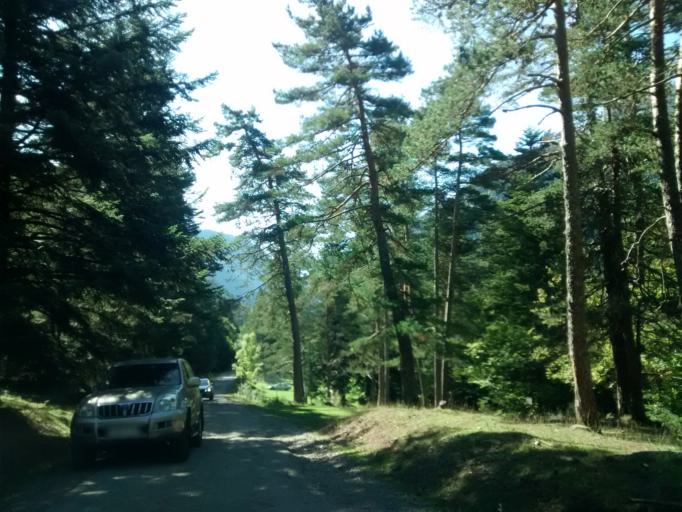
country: ES
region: Aragon
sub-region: Provincia de Huesca
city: Aragues del Puerto
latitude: 42.8375
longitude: -0.7113
